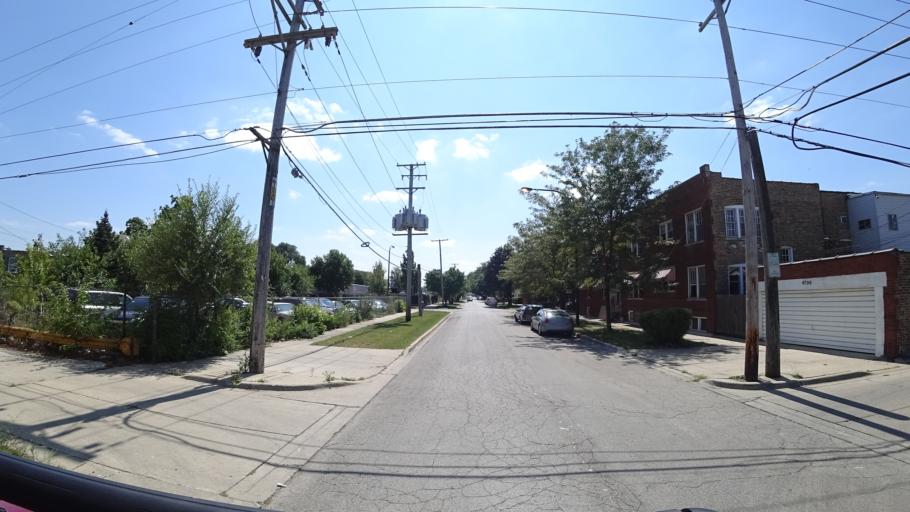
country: US
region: Illinois
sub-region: Cook County
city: Cicero
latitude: 41.8545
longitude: -87.7419
